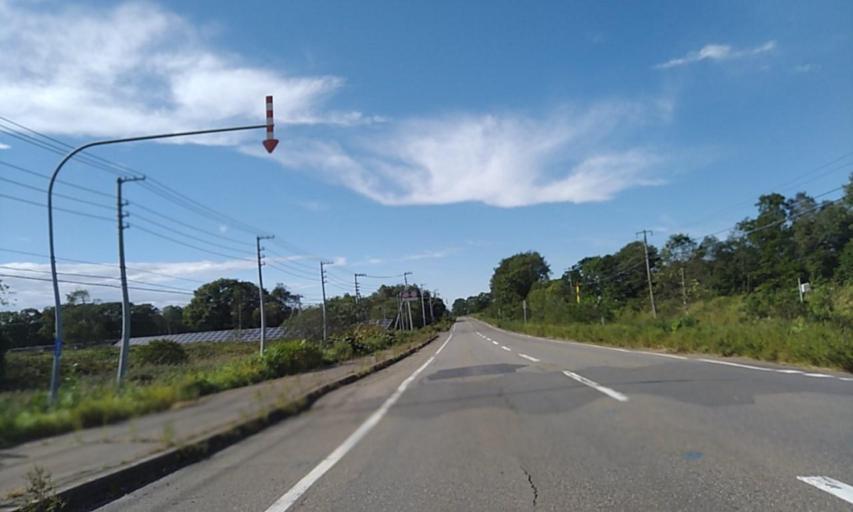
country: JP
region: Hokkaido
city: Obihiro
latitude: 42.8117
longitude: 143.5507
